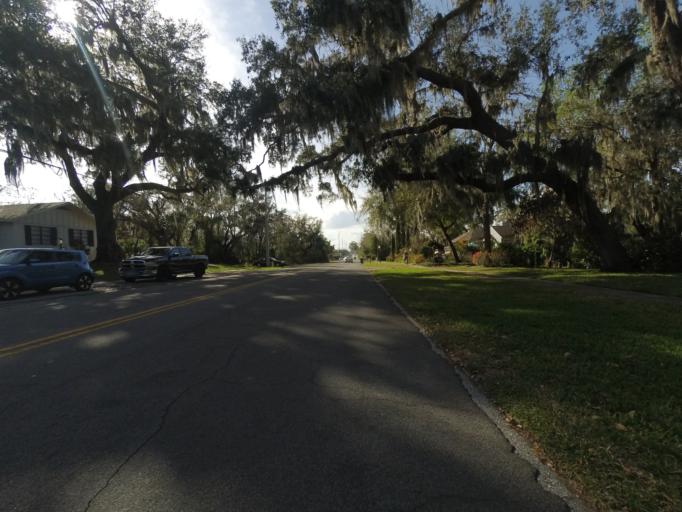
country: US
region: Florida
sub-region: Lake County
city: Mount Dora
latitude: 28.8071
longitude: -81.6586
